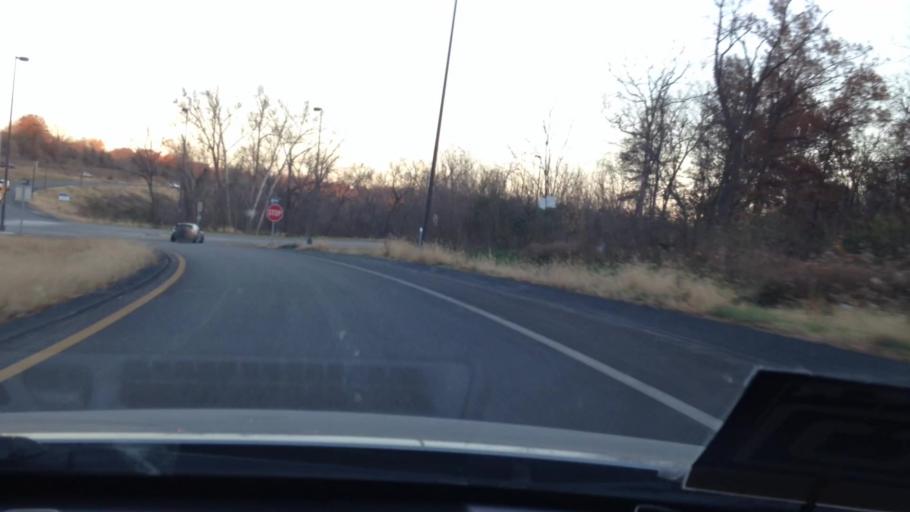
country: US
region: Missouri
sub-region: Clay County
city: Gladstone
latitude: 39.2570
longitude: -94.5590
